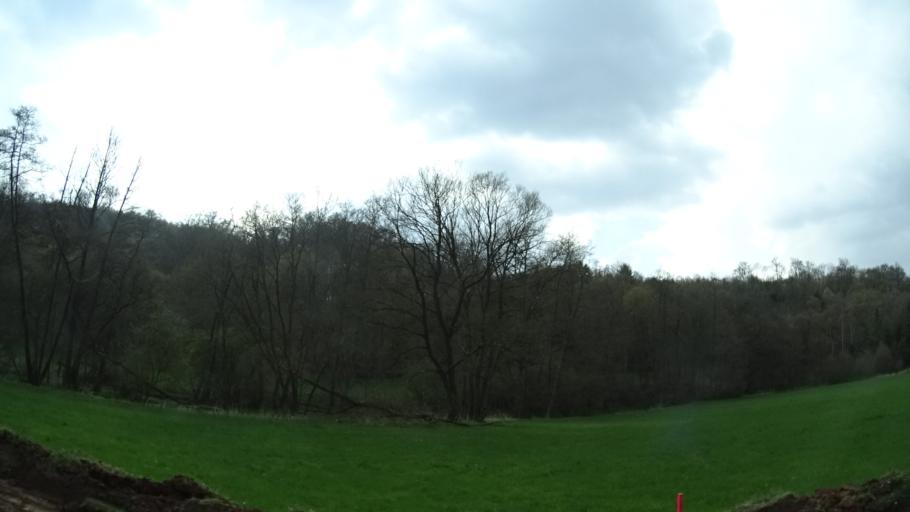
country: DE
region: Rheinland-Pfalz
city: Allenfeld
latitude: 49.8488
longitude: 7.6605
